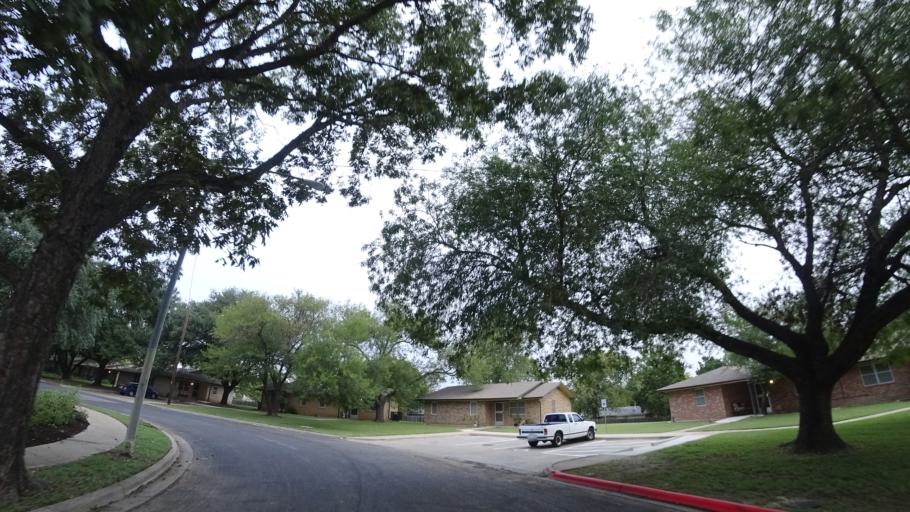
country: US
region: Texas
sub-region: Travis County
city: Onion Creek
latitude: 30.1979
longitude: -97.7791
